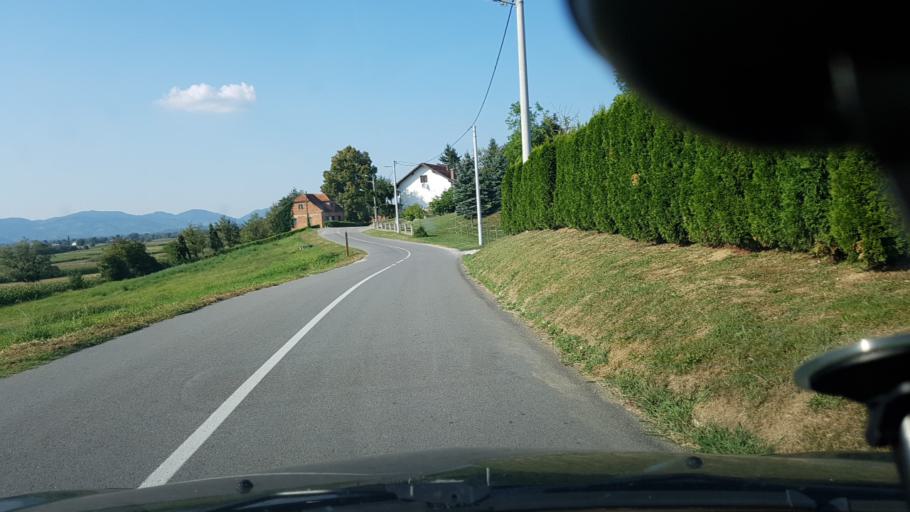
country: HR
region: Zagrebacka
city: Pojatno
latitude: 45.9379
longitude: 15.7276
